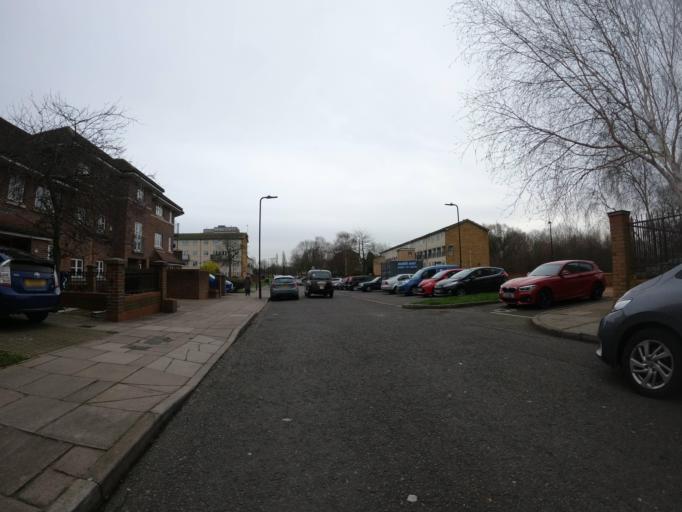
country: GB
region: England
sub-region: Greater London
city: Greenford
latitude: 51.5159
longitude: -0.3592
